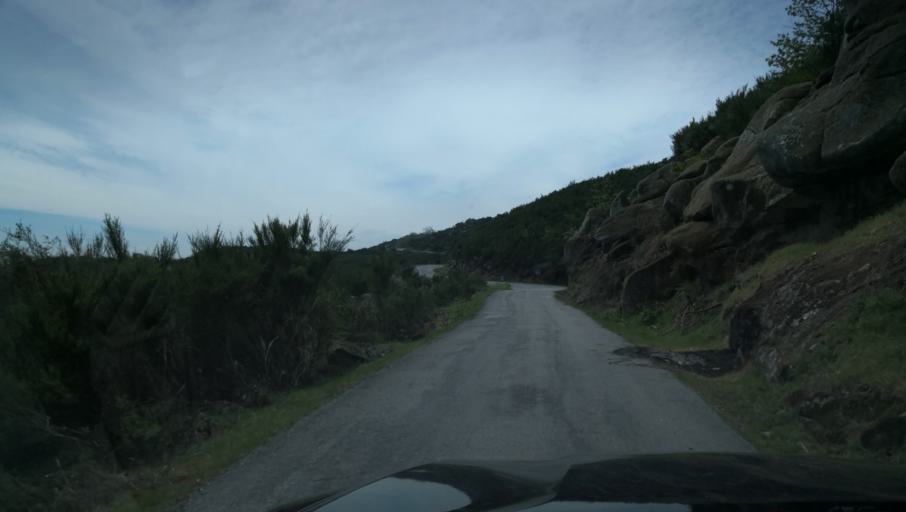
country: PT
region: Vila Real
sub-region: Vila Real
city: Vila Real
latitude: 41.3041
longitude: -7.8099
